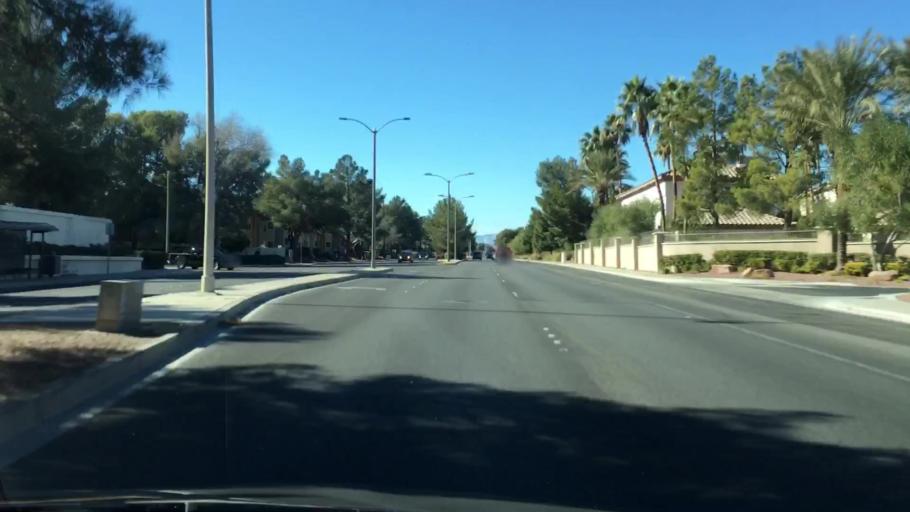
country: US
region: Nevada
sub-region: Clark County
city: Whitney
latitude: 36.0564
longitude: -115.0776
